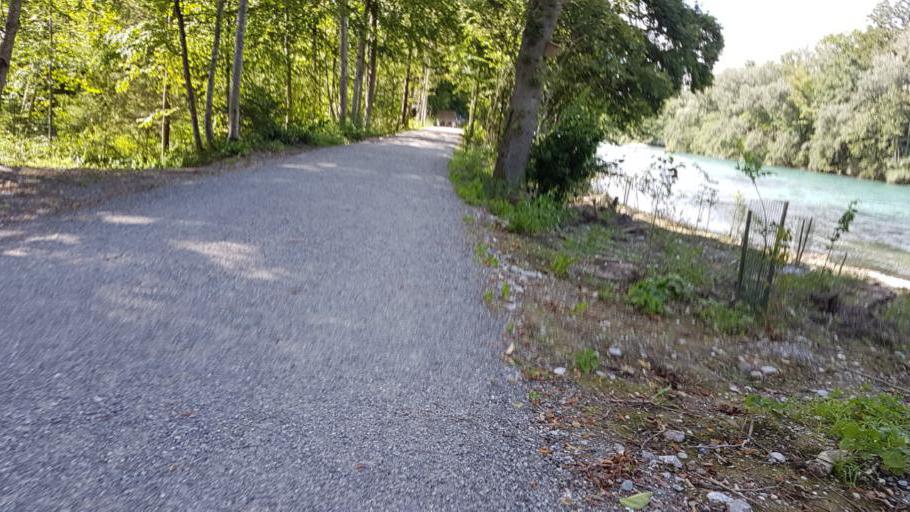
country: CH
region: Bern
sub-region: Bern-Mittelland District
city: Rubigen
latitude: 46.8933
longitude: 7.5338
